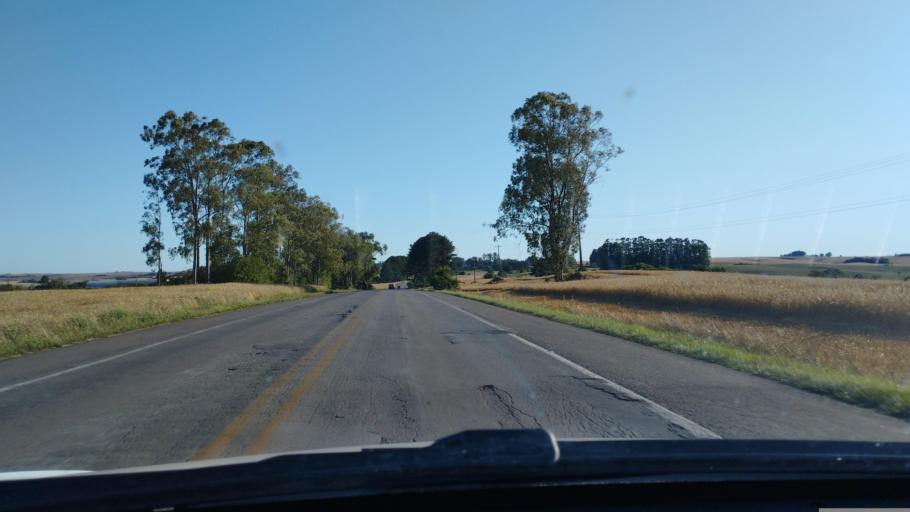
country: BR
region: Rio Grande do Sul
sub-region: Julio De Castilhos
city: Julio de Castilhos
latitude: -29.4281
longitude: -53.6744
